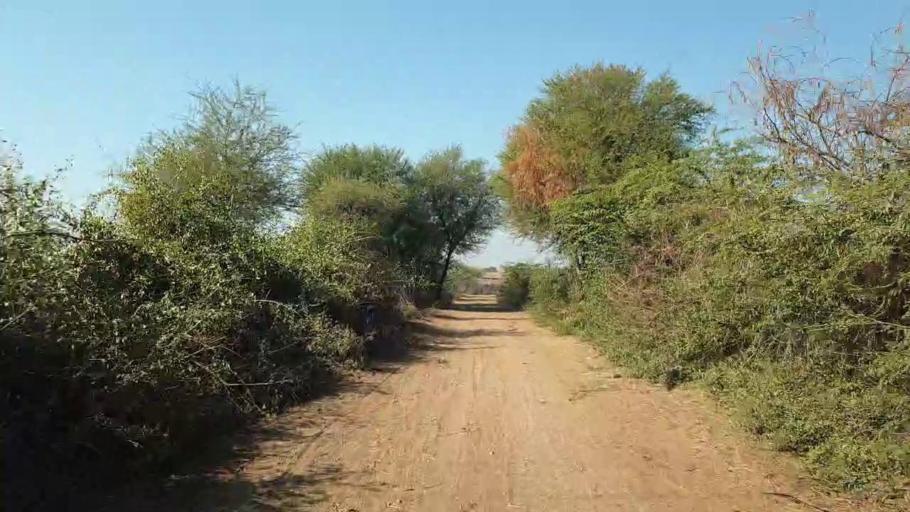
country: PK
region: Sindh
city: Nawabshah
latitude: 26.0660
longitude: 68.4759
